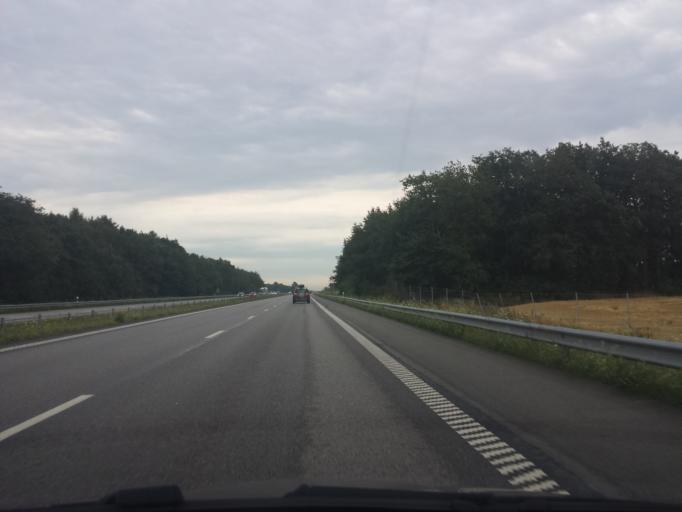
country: SE
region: Skane
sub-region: Malmo
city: Oxie
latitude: 55.5471
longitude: 13.1391
